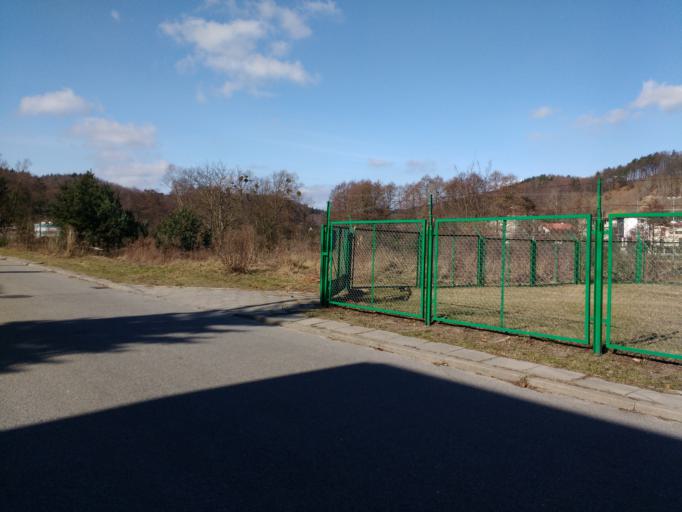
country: PL
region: Pomeranian Voivodeship
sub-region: Gdynia
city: Wielki Kack
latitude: 54.4833
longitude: 18.5178
